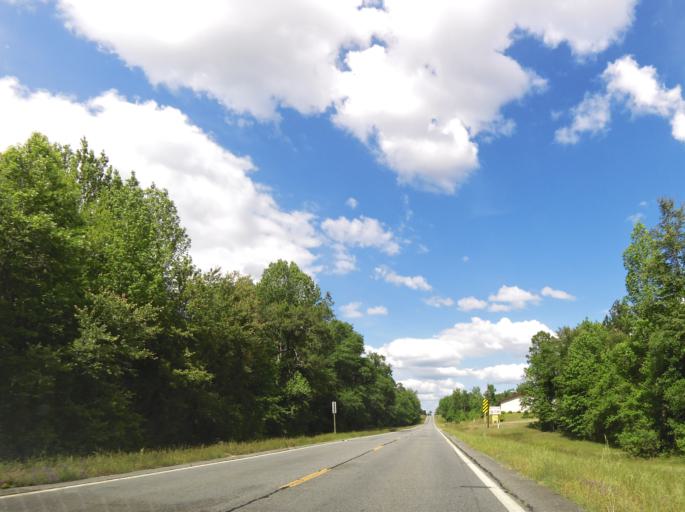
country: US
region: Georgia
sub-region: Treutlen County
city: Soperton
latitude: 32.3609
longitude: -82.6225
